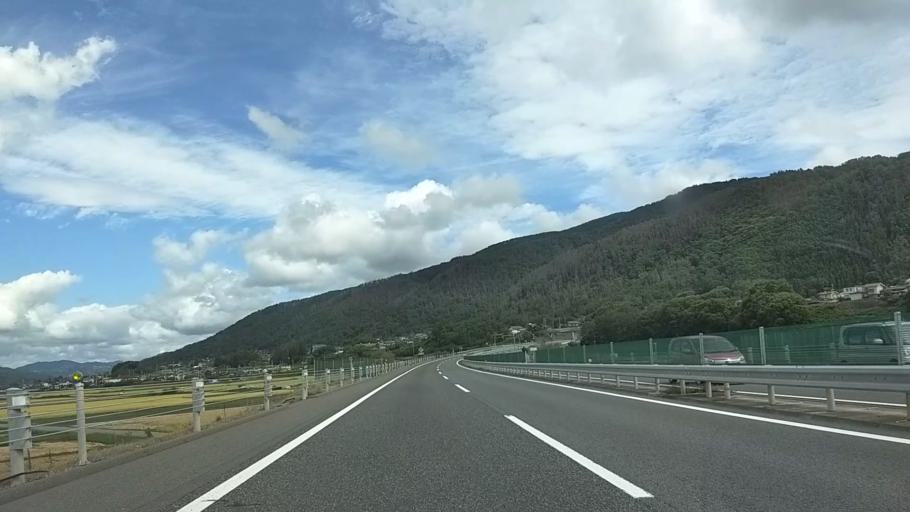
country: JP
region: Nagano
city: Toyoshina
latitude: 36.3240
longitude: 137.9231
